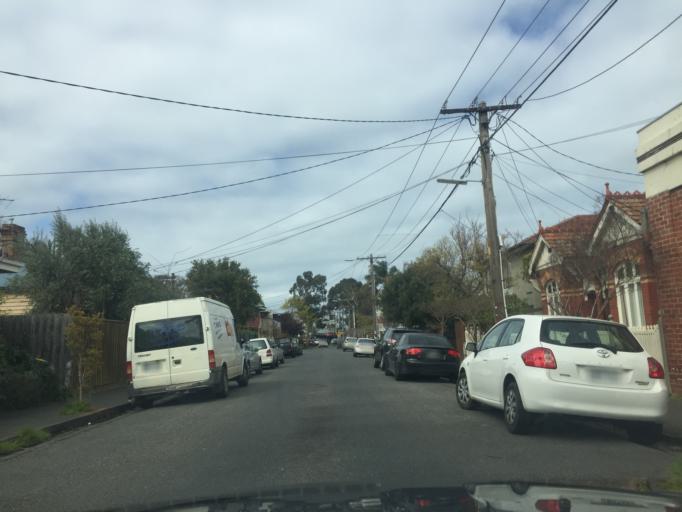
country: AU
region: Victoria
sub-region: Port Phillip
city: Balaclava
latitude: -37.8667
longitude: 144.9937
